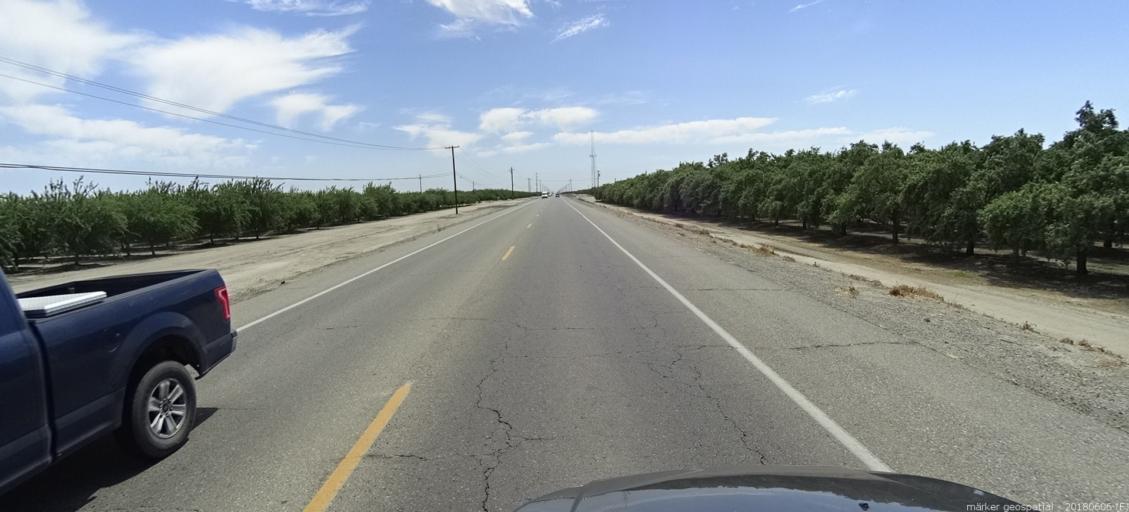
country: US
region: California
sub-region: Fresno County
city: Firebaugh
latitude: 36.8585
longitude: -120.4022
